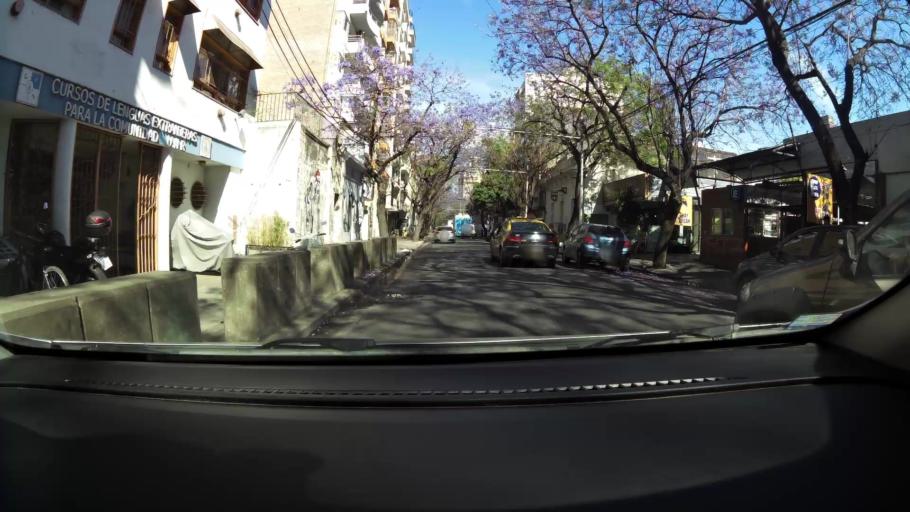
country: AR
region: Santa Fe
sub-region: Departamento de Rosario
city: Rosario
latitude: -32.9490
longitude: -60.6452
